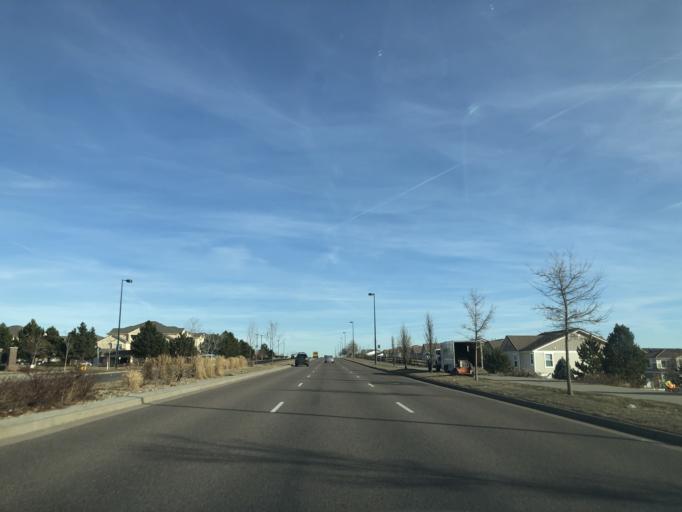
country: US
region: Colorado
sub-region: Adams County
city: Aurora
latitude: 39.7983
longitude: -104.7592
